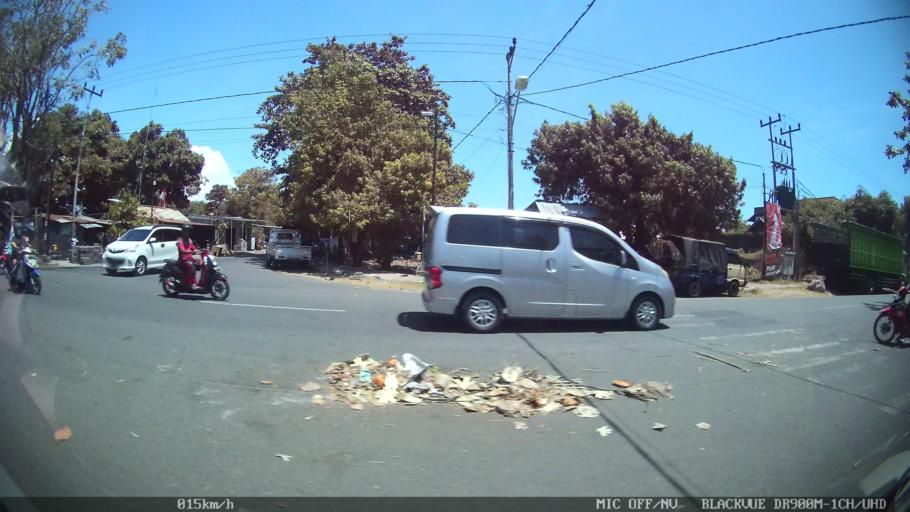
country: ID
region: Bali
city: Banjar Kampunganyar
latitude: -8.1081
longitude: 115.0835
